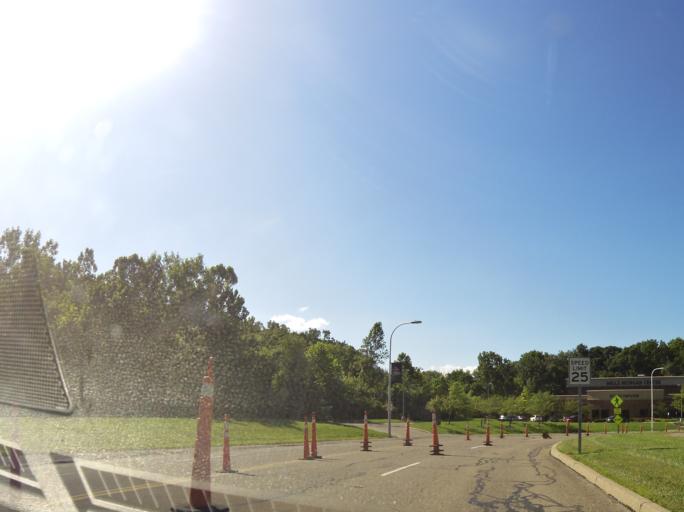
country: US
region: Ohio
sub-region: Greene County
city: Wright-Patterson AFB
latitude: 39.7811
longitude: -84.0544
